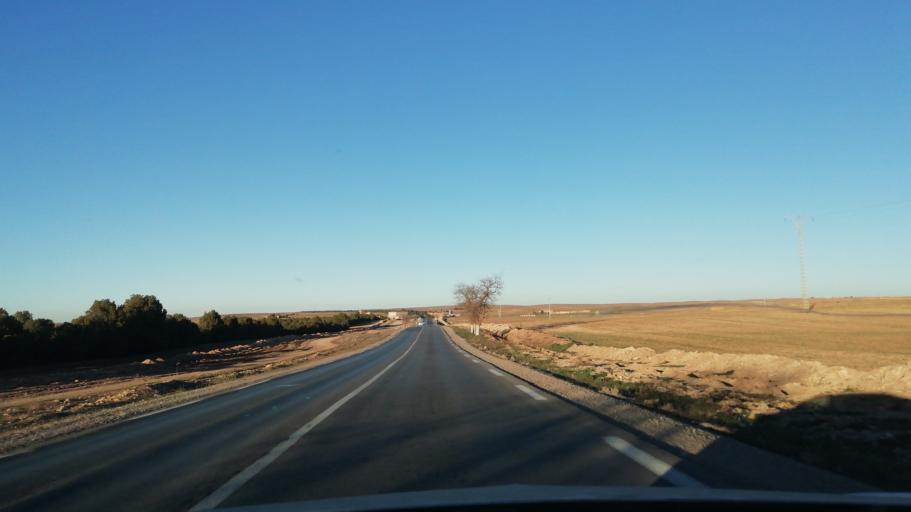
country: DZ
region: Saida
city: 'Ain el Hadjar
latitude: 34.5689
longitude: 0.1234
